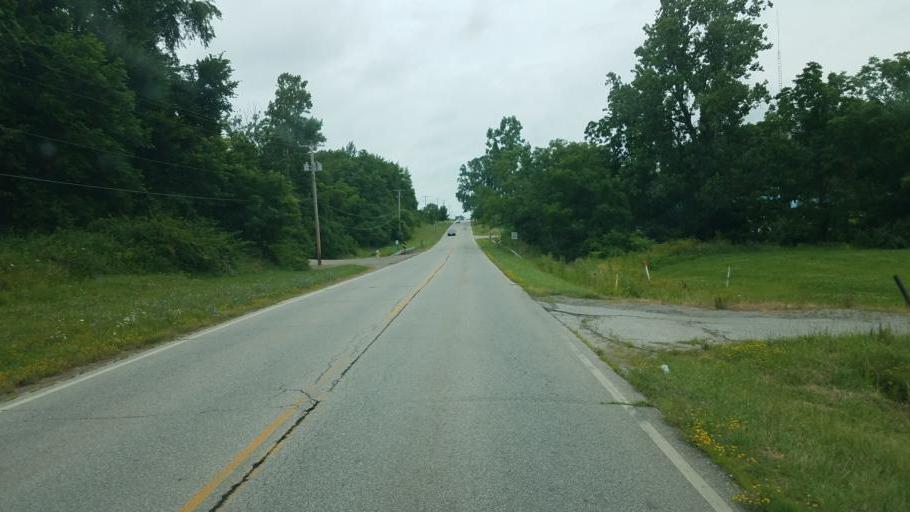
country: US
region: Ohio
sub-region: Richland County
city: Ontario
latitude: 40.7817
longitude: -82.5708
